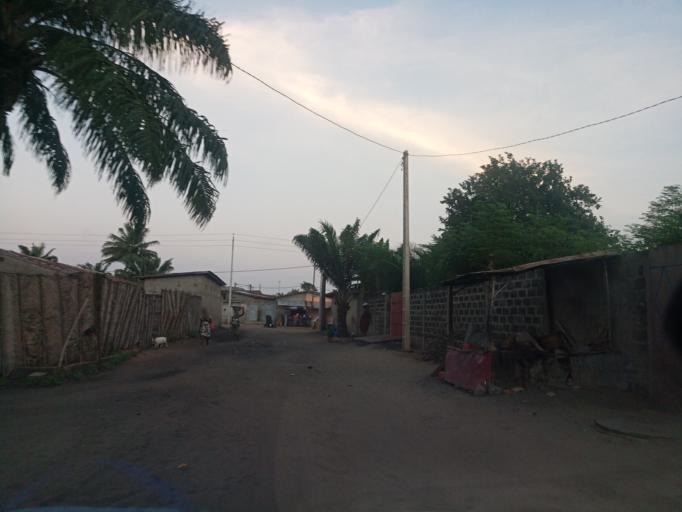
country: BJ
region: Atlantique
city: Hevie
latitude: 6.3927
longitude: 2.2901
